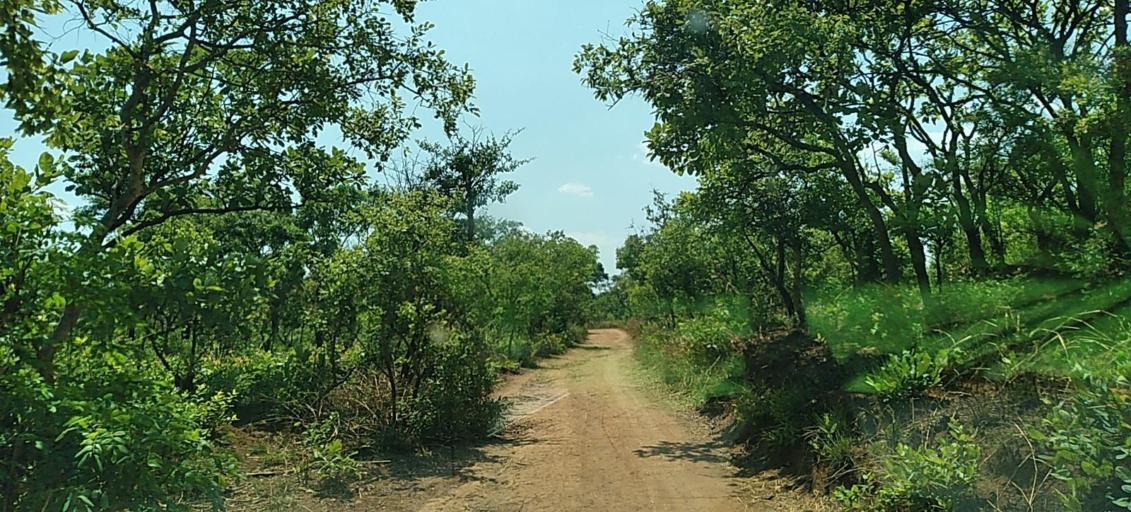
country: CD
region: Katanga
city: Kolwezi
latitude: -11.2887
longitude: 25.2005
